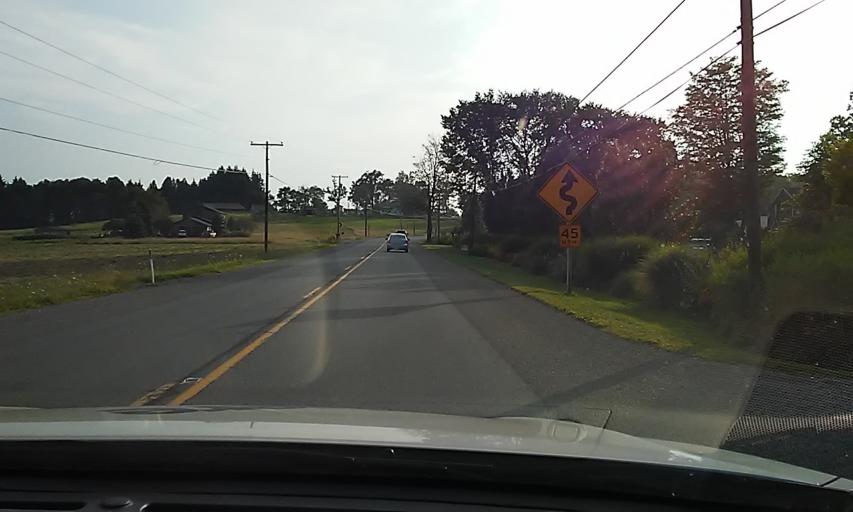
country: US
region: Pennsylvania
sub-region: McKean County
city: Kane
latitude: 41.7000
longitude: -78.7083
